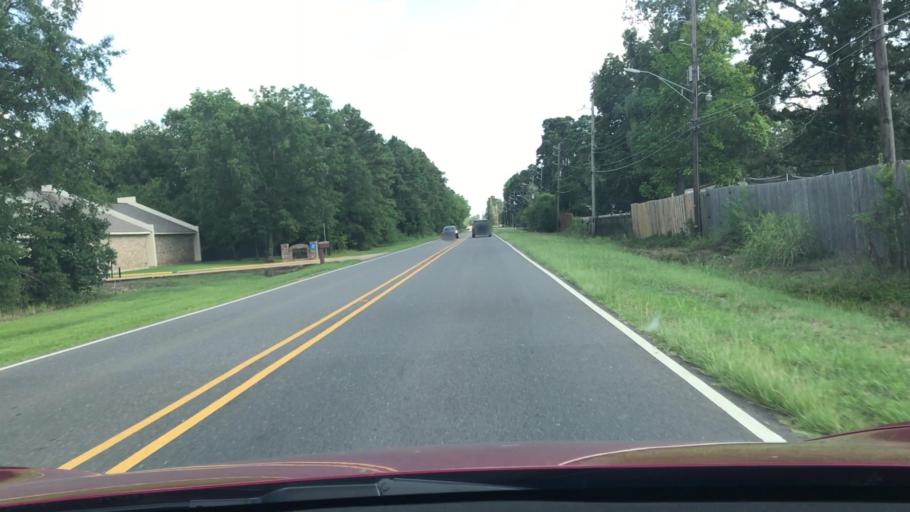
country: US
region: Louisiana
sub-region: Bossier Parish
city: Bossier City
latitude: 32.3961
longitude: -93.7386
